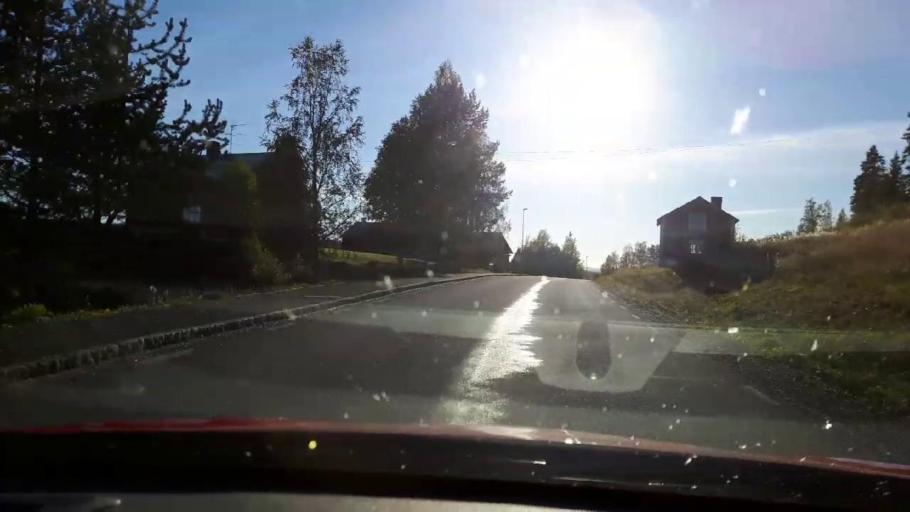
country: SE
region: Jaemtland
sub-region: OEstersunds Kommun
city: Lit
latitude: 63.8114
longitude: 14.7937
